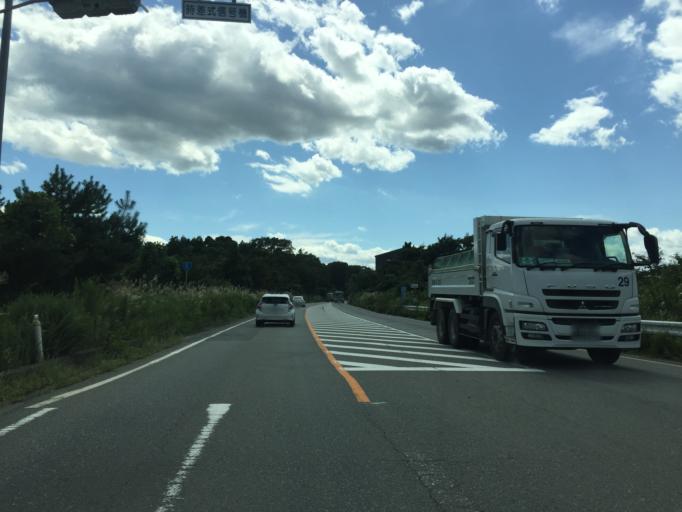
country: JP
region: Fukushima
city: Namie
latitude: 37.4346
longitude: 141.0111
